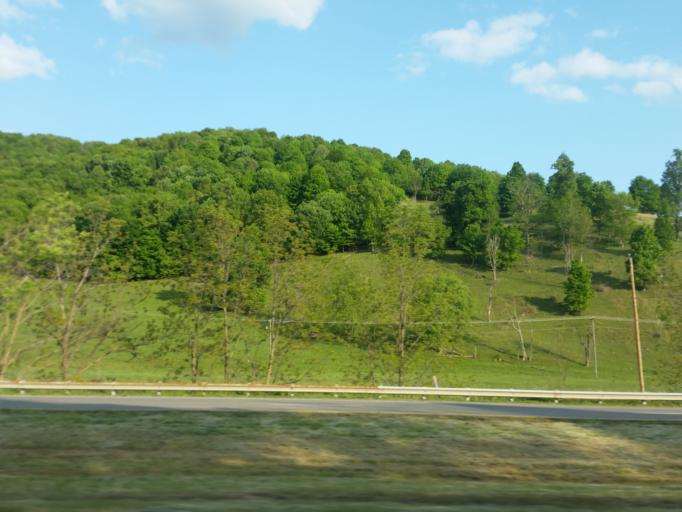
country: US
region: Virginia
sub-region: Russell County
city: Honaker
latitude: 36.9460
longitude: -81.9575
